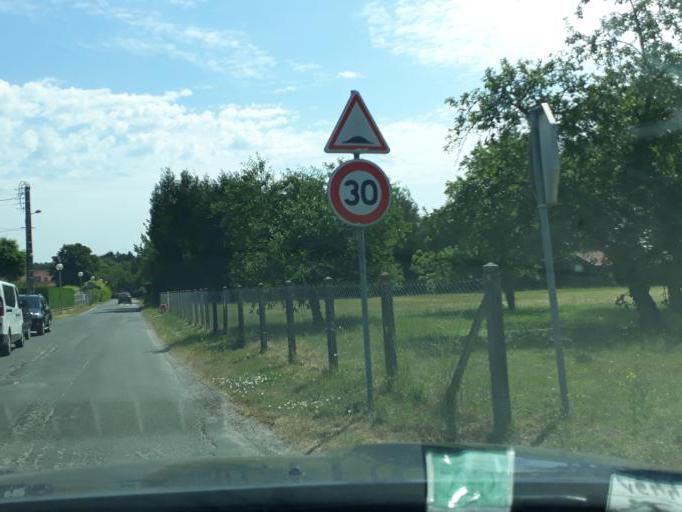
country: FR
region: Centre
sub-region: Departement du Loir-et-Cher
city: Vouzon
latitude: 47.6478
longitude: 2.0544
